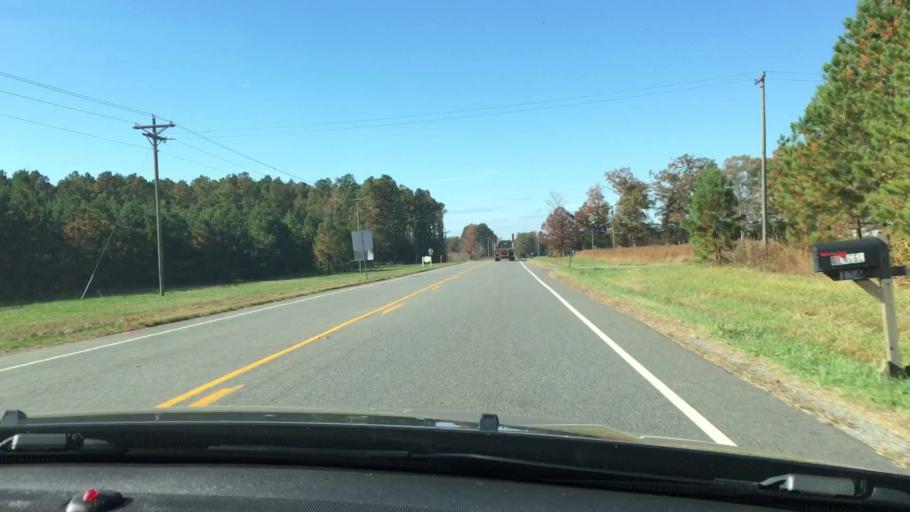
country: US
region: Virginia
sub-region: Hanover County
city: Hanover
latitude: 37.8157
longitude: -77.3139
